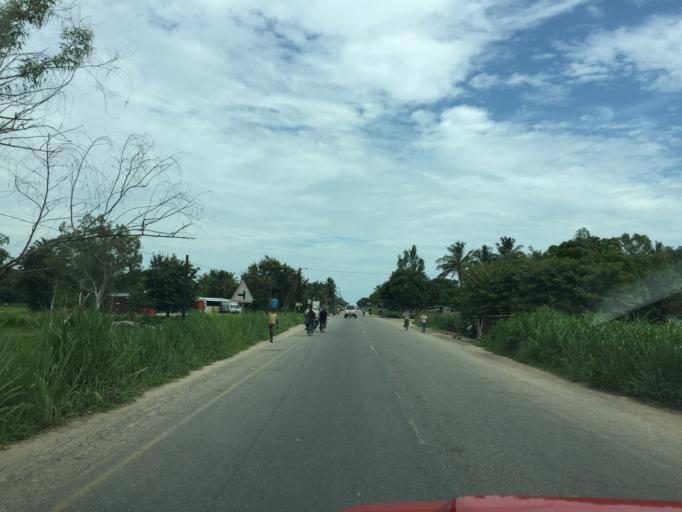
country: MZ
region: Zambezia
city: Quelimane
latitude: -17.6000
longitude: 36.8180
